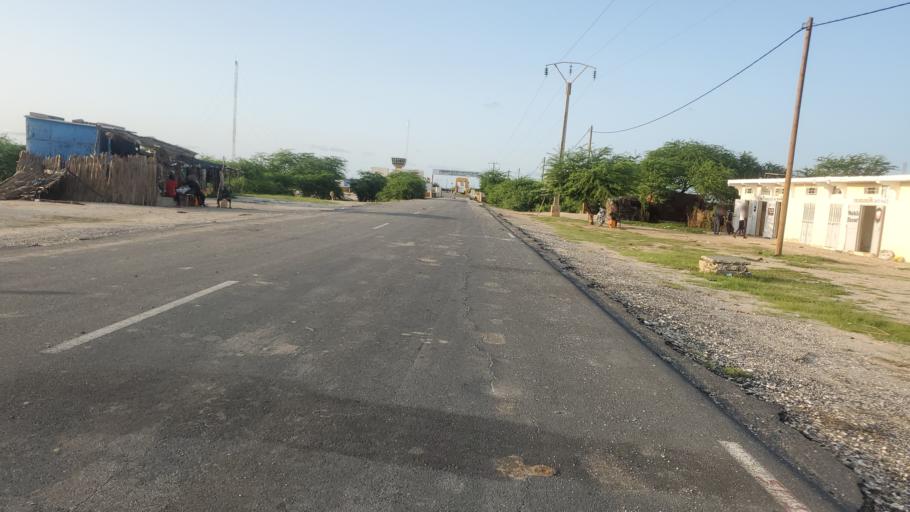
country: SN
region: Saint-Louis
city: Saint-Louis
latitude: 16.2117
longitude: -16.4153
